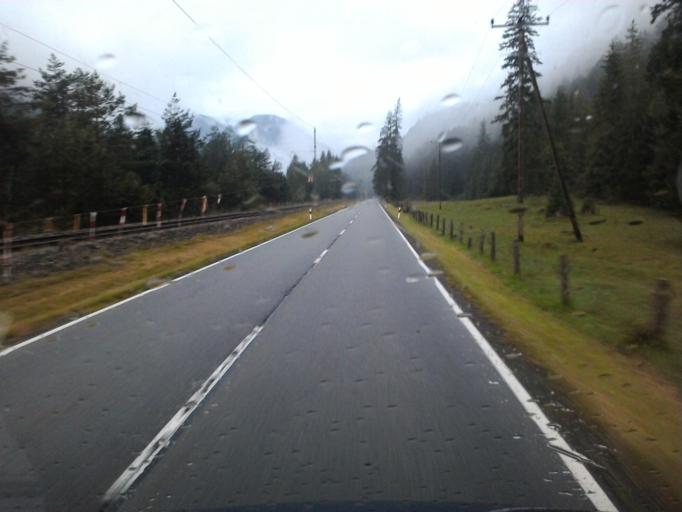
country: DE
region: Bavaria
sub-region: Upper Bavaria
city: Grainau
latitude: 47.4803
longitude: 10.9611
